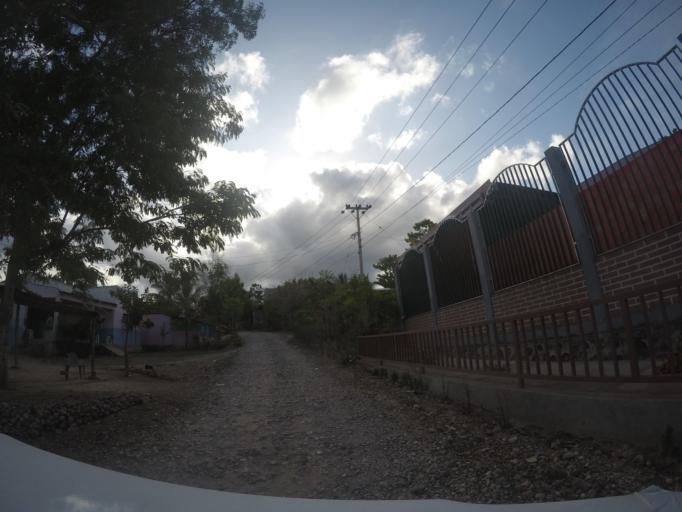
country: TL
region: Baucau
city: Baucau
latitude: -8.4756
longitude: 126.4598
